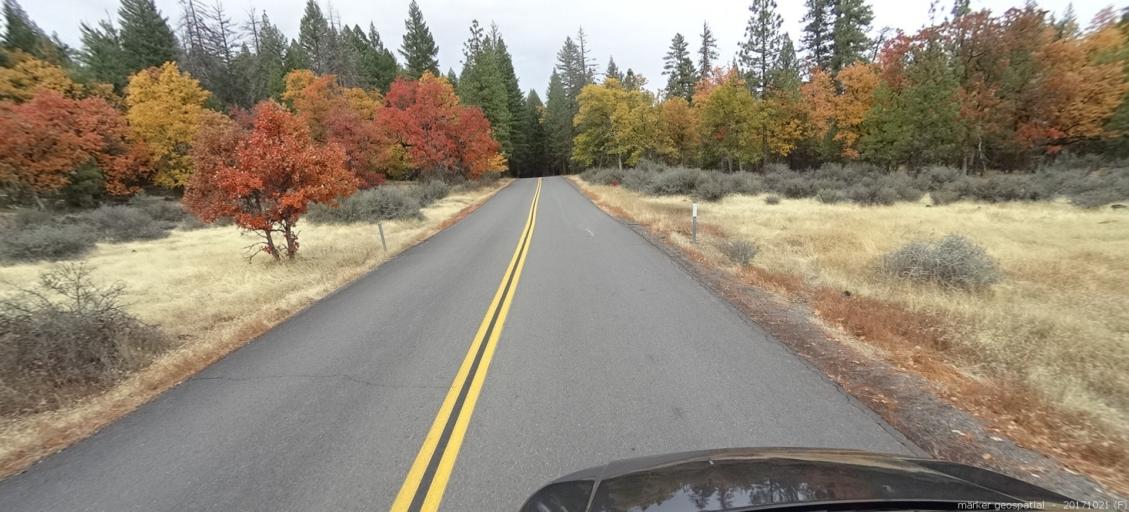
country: US
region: California
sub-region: Shasta County
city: Burney
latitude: 41.0147
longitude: -121.6557
